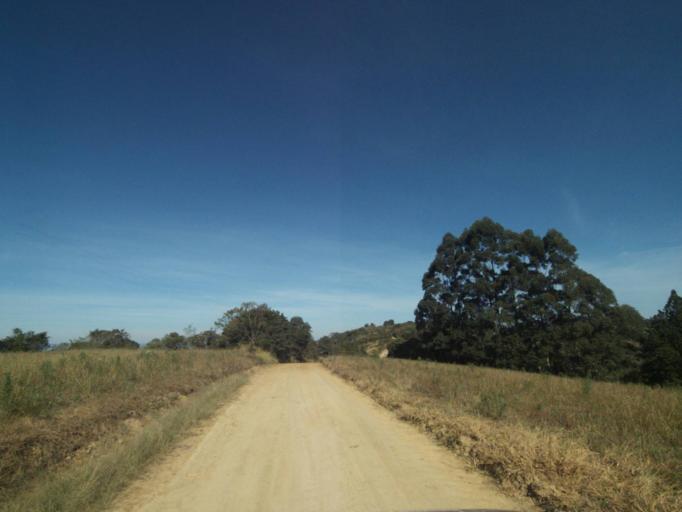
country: BR
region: Parana
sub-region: Tibagi
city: Tibagi
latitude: -24.5619
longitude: -50.4721
